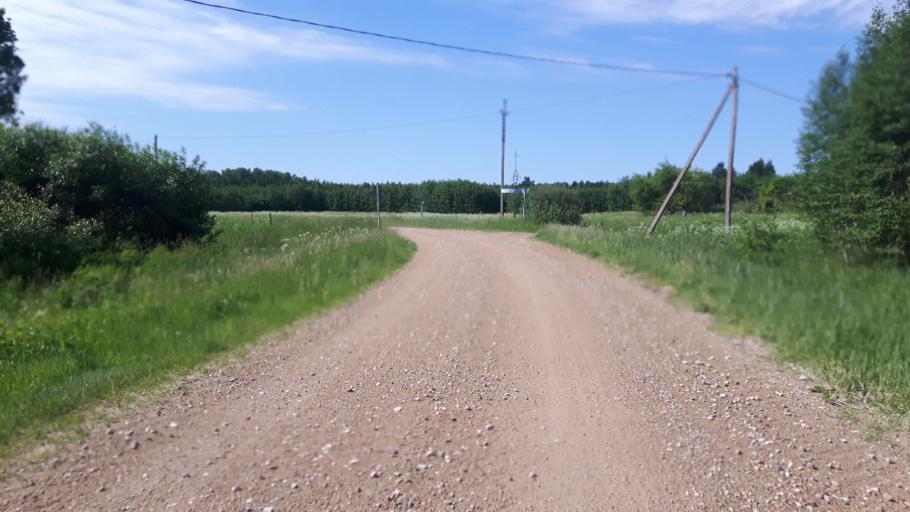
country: EE
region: Paernumaa
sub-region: Vaendra vald (alev)
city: Vandra
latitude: 58.7037
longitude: 25.0288
